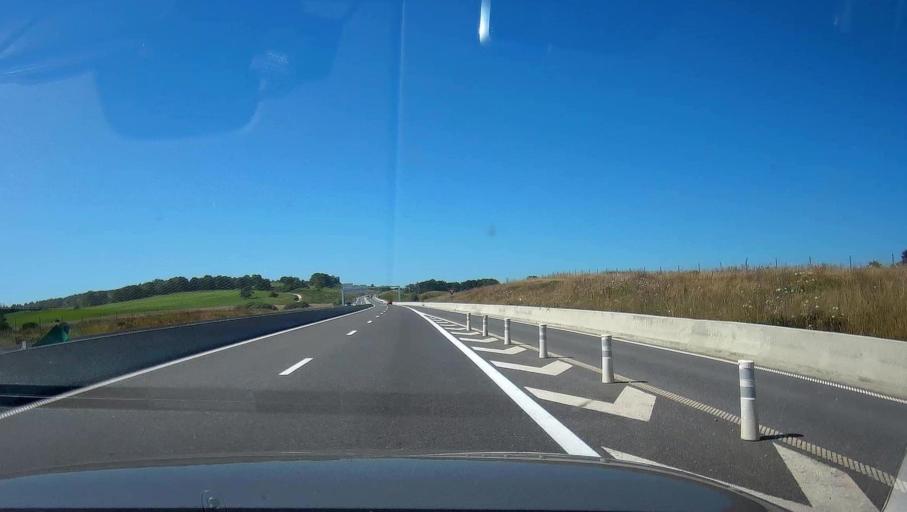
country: FR
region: Champagne-Ardenne
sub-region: Departement des Ardennes
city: Tournes
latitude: 49.7666
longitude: 4.6400
